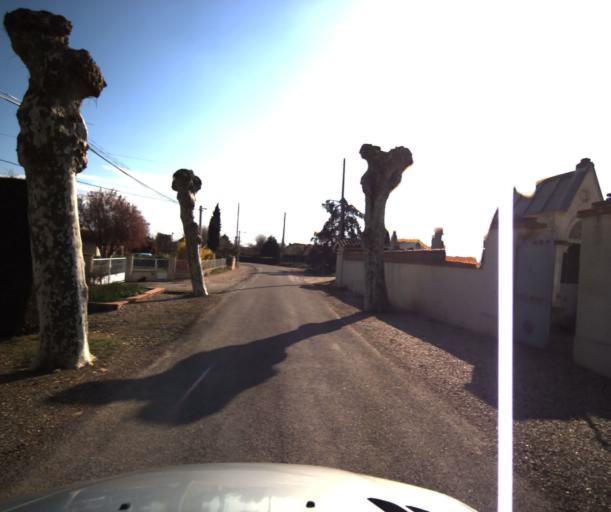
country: FR
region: Midi-Pyrenees
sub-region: Departement du Tarn-et-Garonne
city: Bressols
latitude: 43.9381
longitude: 1.3053
